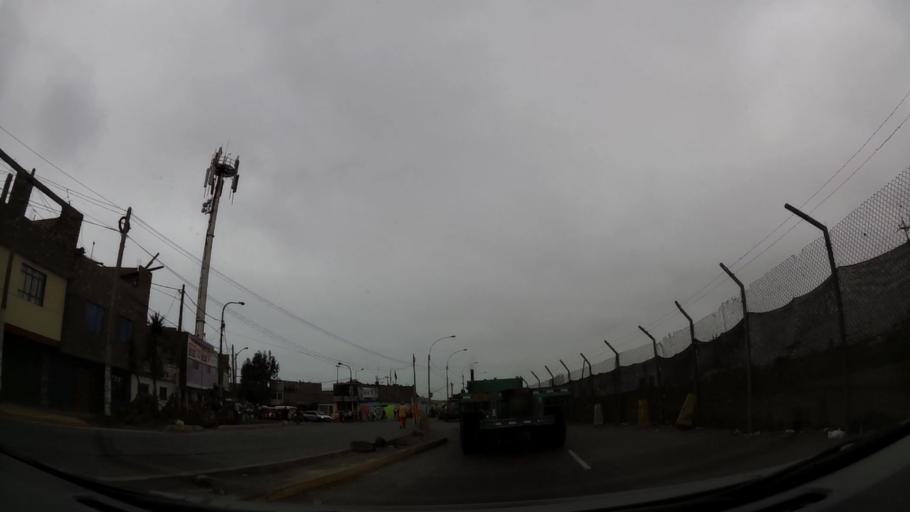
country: PE
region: Callao
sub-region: Callao
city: Callao
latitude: -12.0233
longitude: -77.1289
